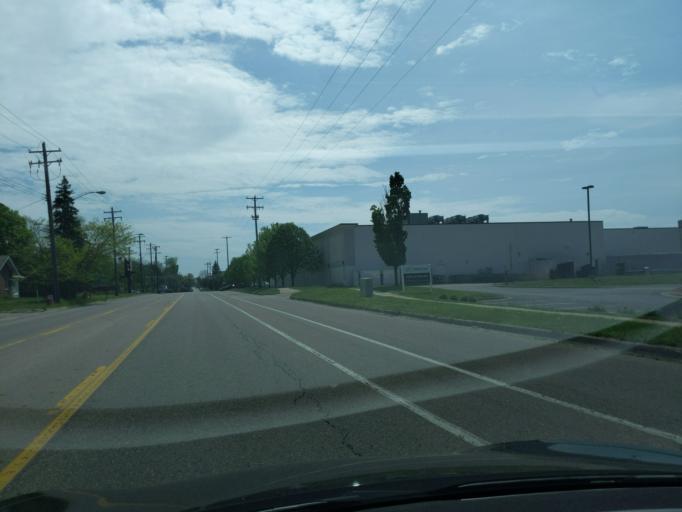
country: US
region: Michigan
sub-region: Ingham County
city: Holt
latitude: 42.6548
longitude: -84.5354
